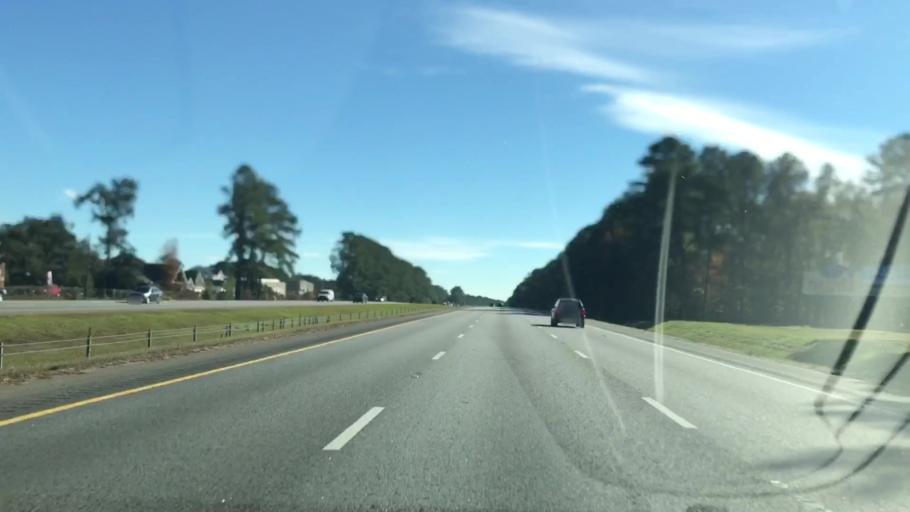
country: US
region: South Carolina
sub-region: Berkeley County
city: Sangaree
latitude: 33.0153
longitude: -80.1191
